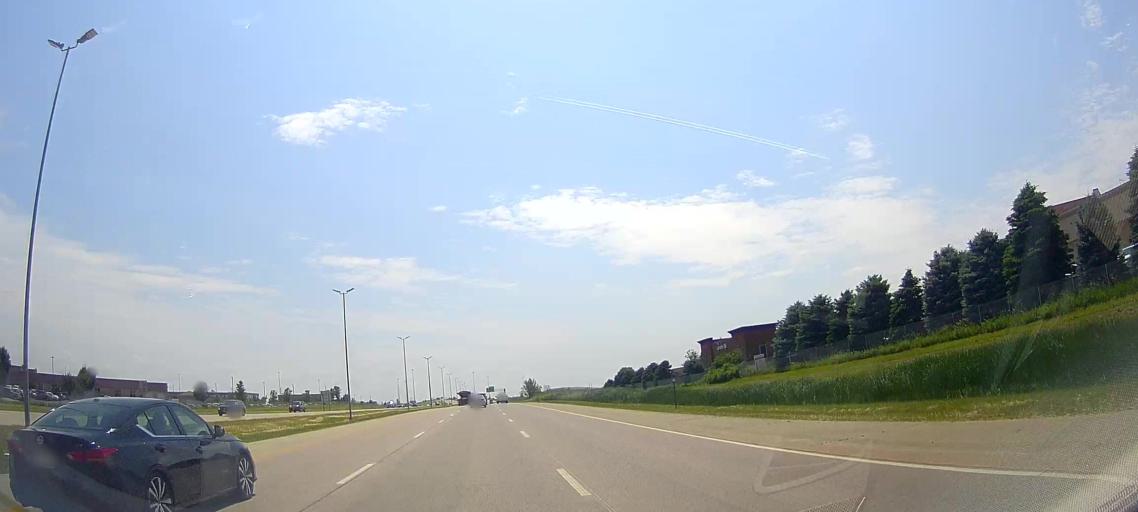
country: US
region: South Dakota
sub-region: Lincoln County
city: Tea
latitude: 43.4993
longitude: -96.7889
